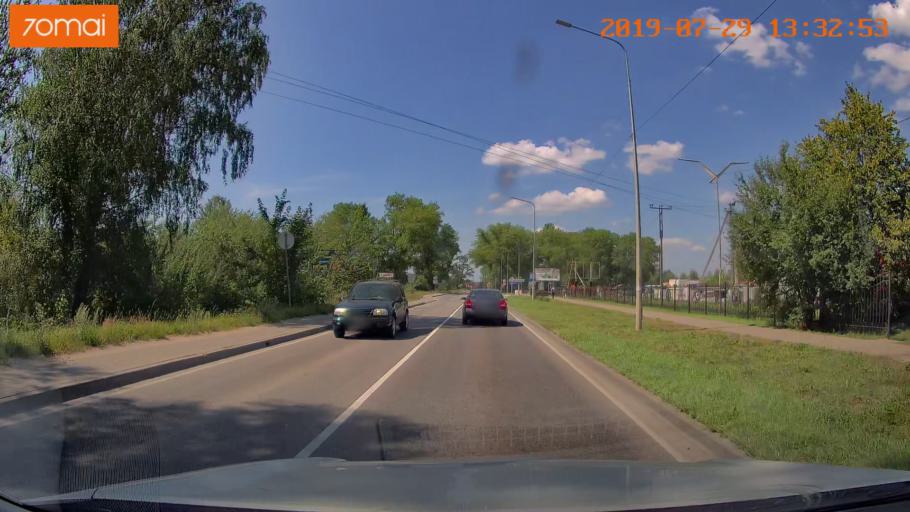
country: RU
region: Kaliningrad
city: Vzmorye
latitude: 54.6981
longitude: 20.2317
